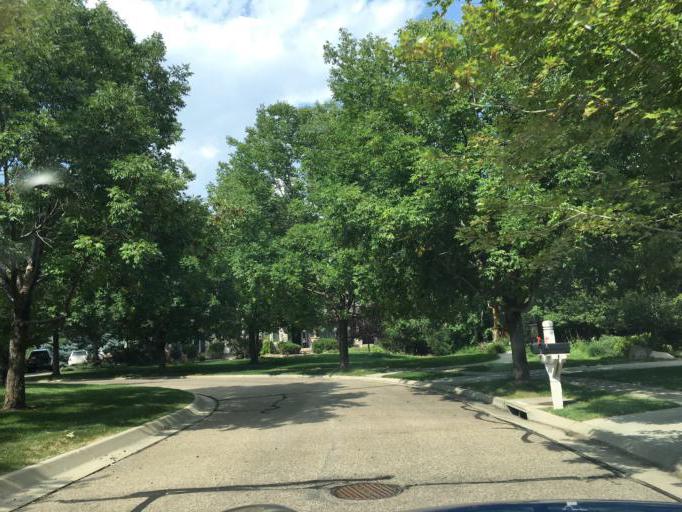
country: US
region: Colorado
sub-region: Boulder County
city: Lafayette
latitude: 40.0210
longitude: -105.1180
